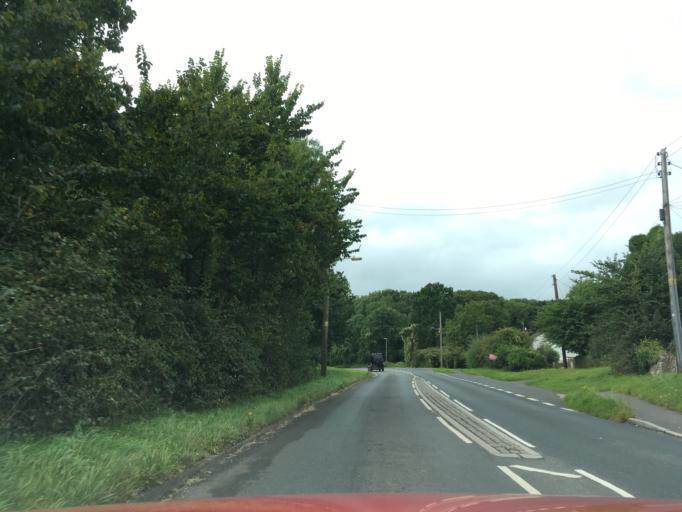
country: GB
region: England
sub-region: South Gloucestershire
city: Tytherington
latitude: 51.5952
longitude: -2.4826
